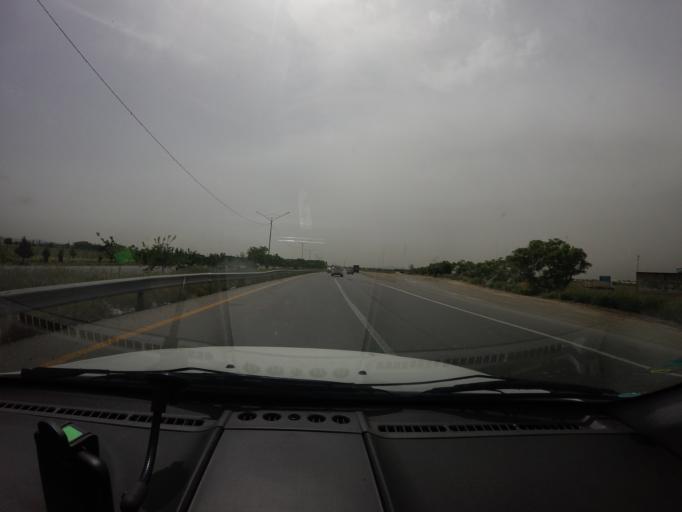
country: IR
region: Tehran
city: Eslamshahr
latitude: 35.6117
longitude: 51.2441
